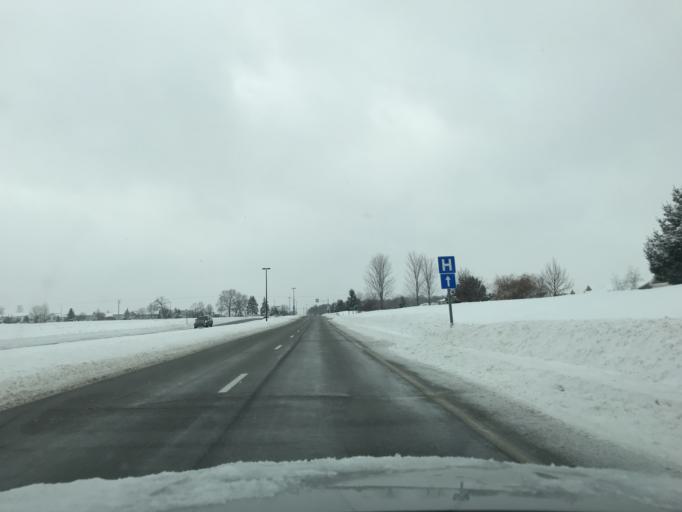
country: US
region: Wisconsin
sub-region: Dane County
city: Sun Prairie
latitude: 43.1650
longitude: -89.2808
